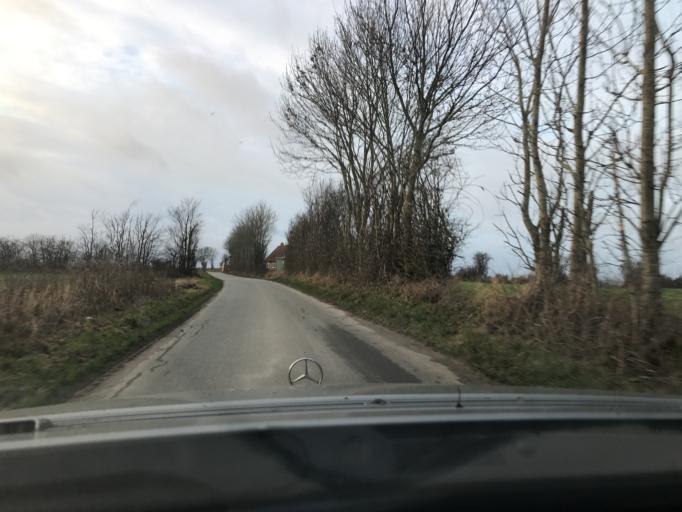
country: DK
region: South Denmark
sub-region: Sonderborg Kommune
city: Nordborg
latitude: 55.0534
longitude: 9.6812
